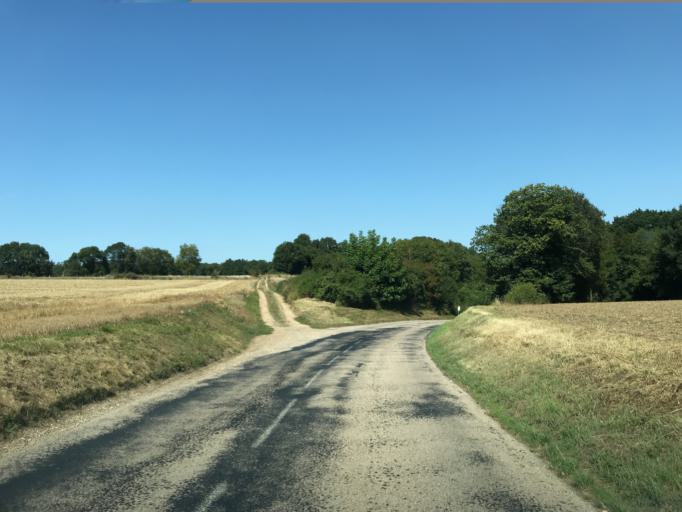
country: FR
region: Haute-Normandie
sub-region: Departement de l'Eure
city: Heudreville-sur-Eure
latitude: 49.1025
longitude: 1.2043
